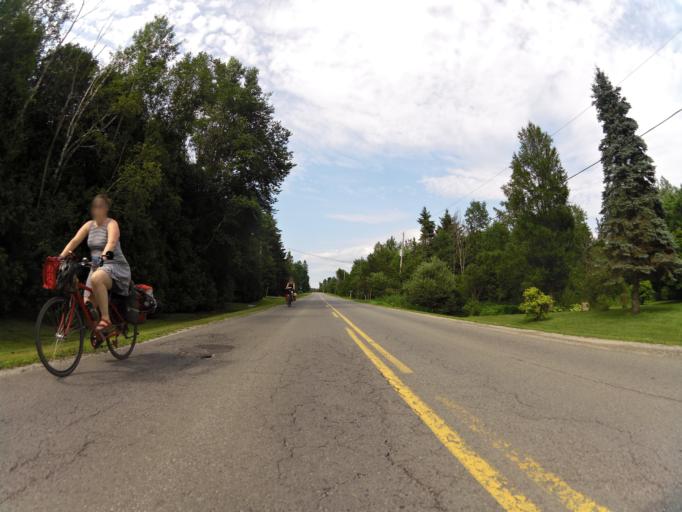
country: CA
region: Ontario
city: Prescott
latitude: 45.0345
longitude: -75.6215
